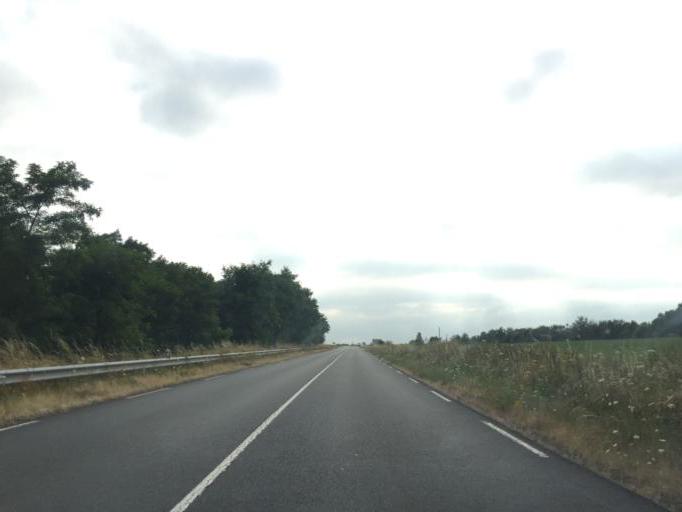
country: FR
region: Auvergne
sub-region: Departement de l'Allier
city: Molinet
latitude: 46.4534
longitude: 3.9213
